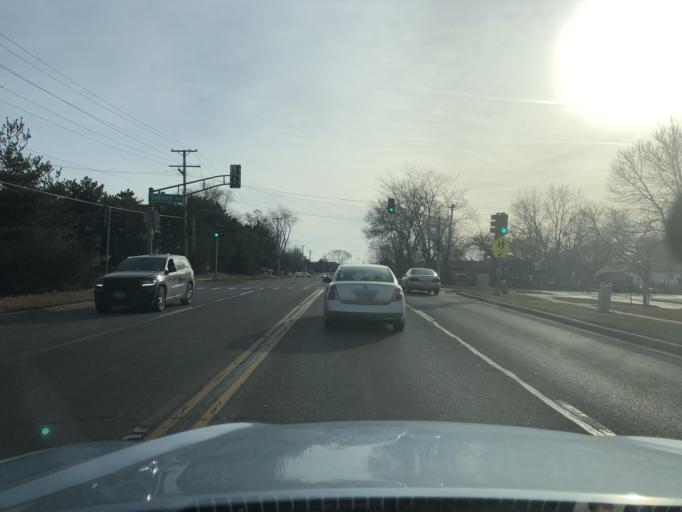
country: US
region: Illinois
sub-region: DuPage County
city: Glendale Heights
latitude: 41.9070
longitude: -88.0815
